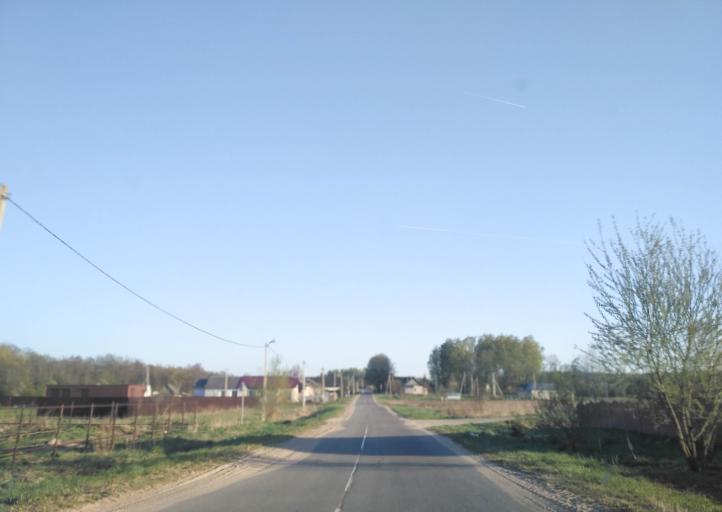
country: BY
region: Minsk
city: Pyatryshki
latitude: 54.1084
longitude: 27.1917
